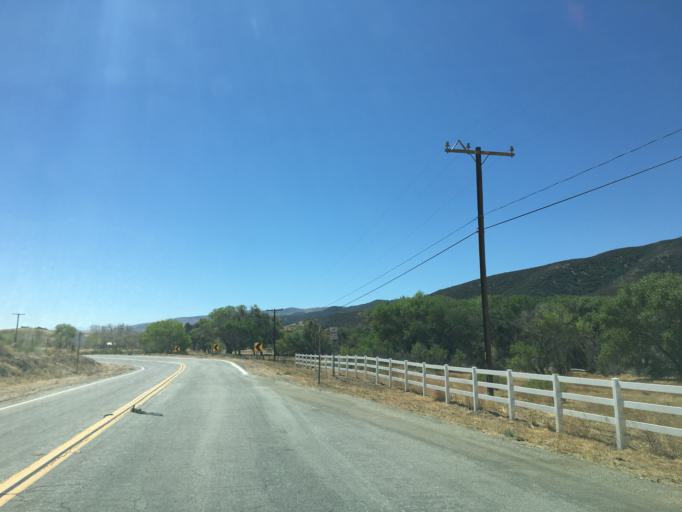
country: US
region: California
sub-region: Los Angeles County
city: Leona Valley
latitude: 34.6312
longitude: -118.3336
